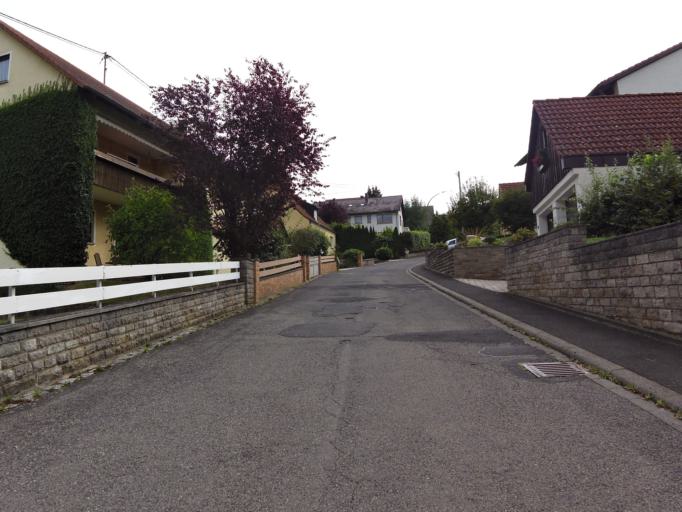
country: DE
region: Bavaria
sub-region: Regierungsbezirk Unterfranken
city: Rimpar
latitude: 49.8445
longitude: 9.9726
